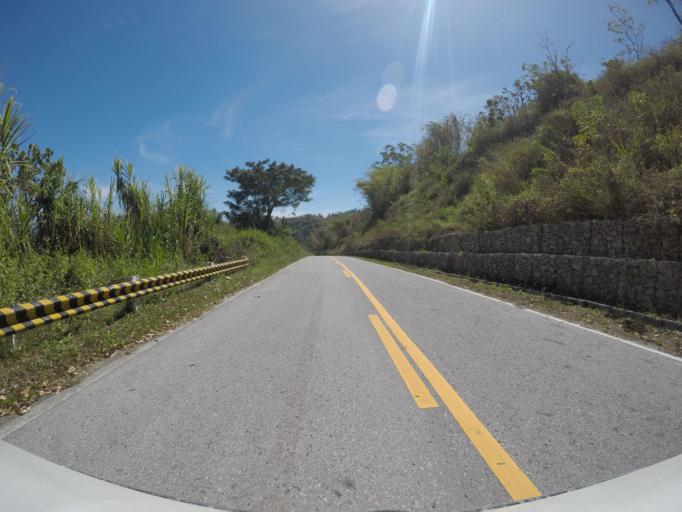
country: TL
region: Manufahi
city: Same
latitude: -8.8826
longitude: 125.9886
